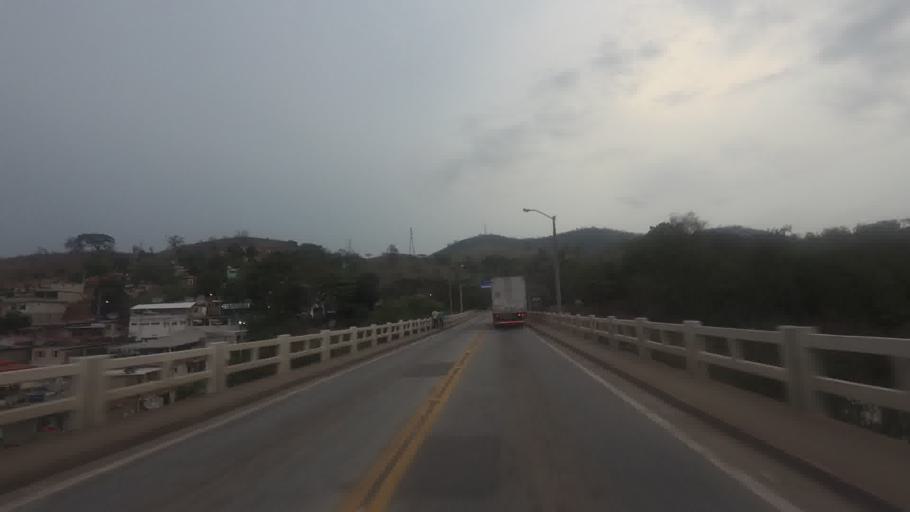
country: BR
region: Minas Gerais
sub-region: Alem Paraiba
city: Alem Paraiba
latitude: -21.8749
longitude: -42.6675
